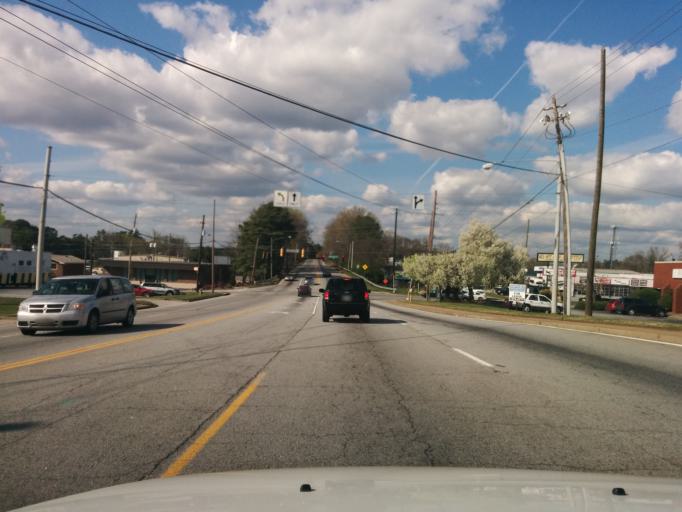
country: US
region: Georgia
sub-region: Fulton County
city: College Park
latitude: 33.6238
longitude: -84.4742
